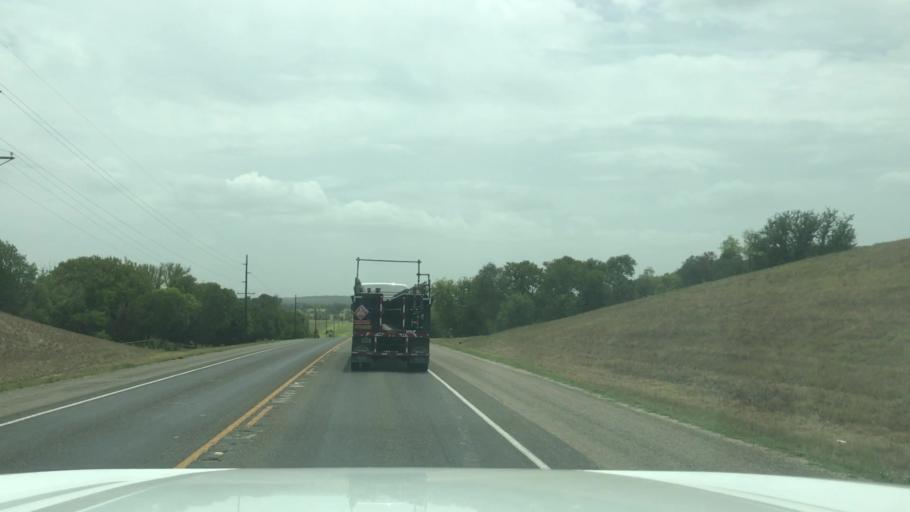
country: US
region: Texas
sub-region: Bosque County
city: Clifton
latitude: 31.7186
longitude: -97.5477
